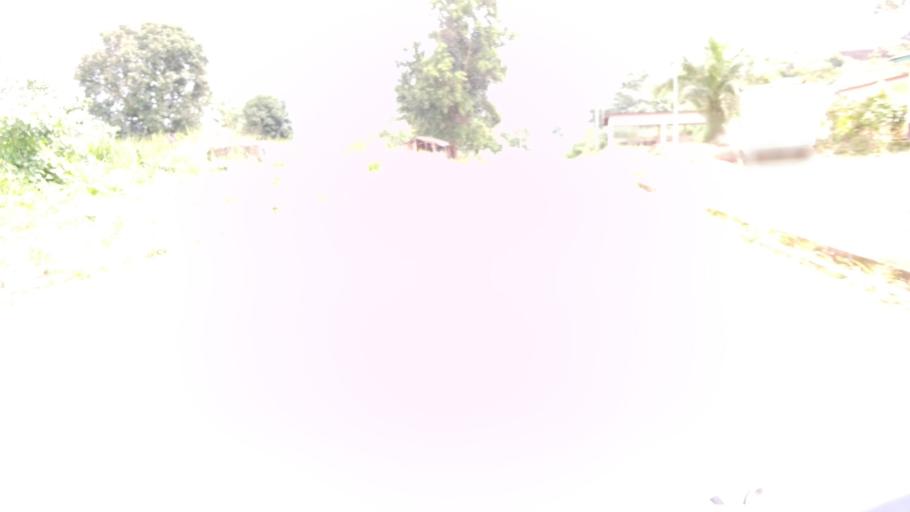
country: SL
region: Eastern Province
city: Koidu
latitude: 8.6548
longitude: -10.9849
